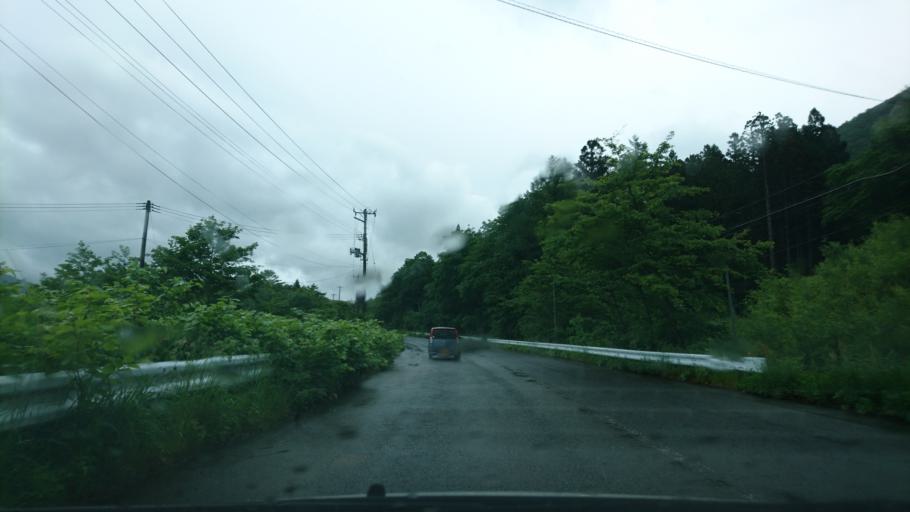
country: JP
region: Iwate
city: Ichinoseki
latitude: 39.0034
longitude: 140.8970
